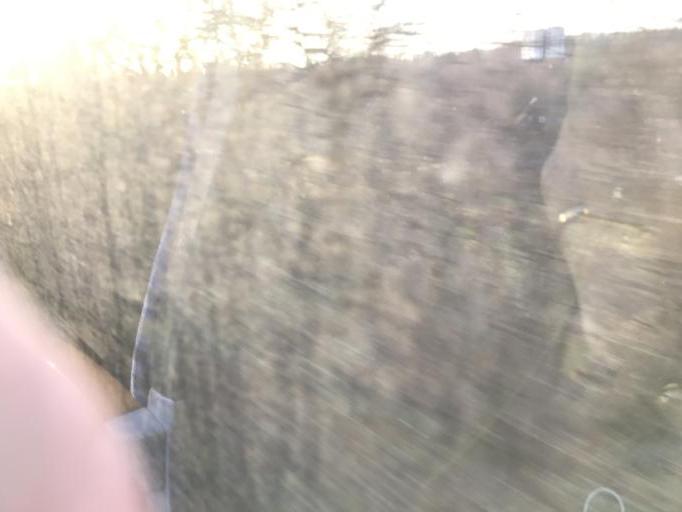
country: DE
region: Schleswig-Holstein
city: Osterronfeld
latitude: 54.3006
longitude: 9.6997
